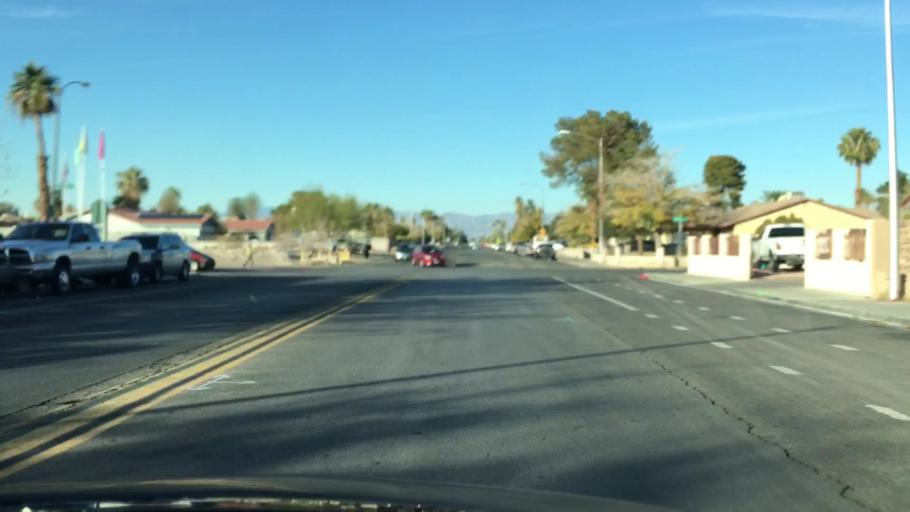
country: US
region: Nevada
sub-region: Clark County
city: Paradise
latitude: 36.0894
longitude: -115.1278
